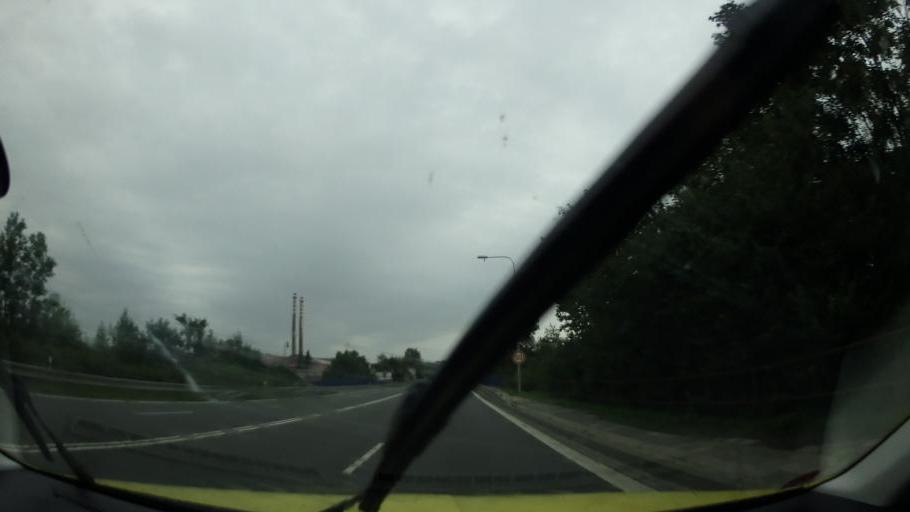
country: CZ
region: Olomoucky
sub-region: Okres Prerov
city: Hranice
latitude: 49.5609
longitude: 17.7559
